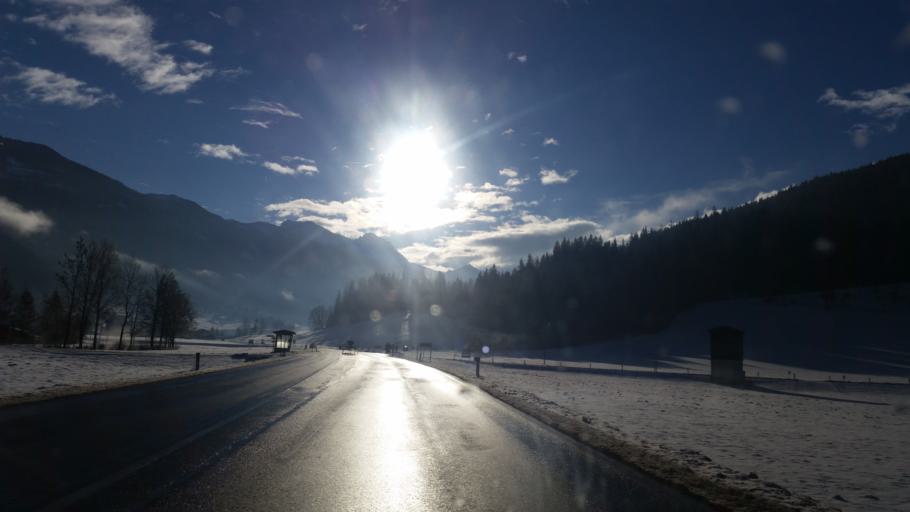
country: AT
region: Salzburg
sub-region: Politischer Bezirk Sankt Johann im Pongau
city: Radstadt
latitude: 47.3698
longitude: 13.4810
